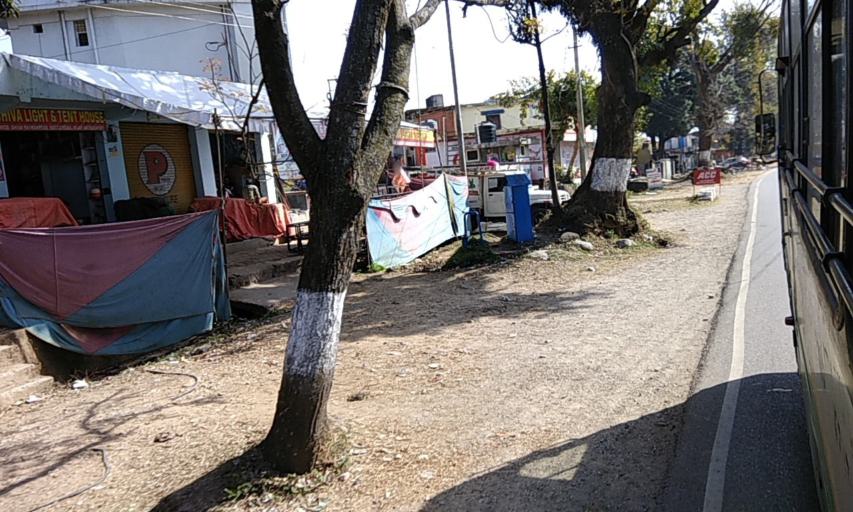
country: IN
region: Himachal Pradesh
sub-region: Kangra
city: Yol
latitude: 32.2202
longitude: 76.1761
